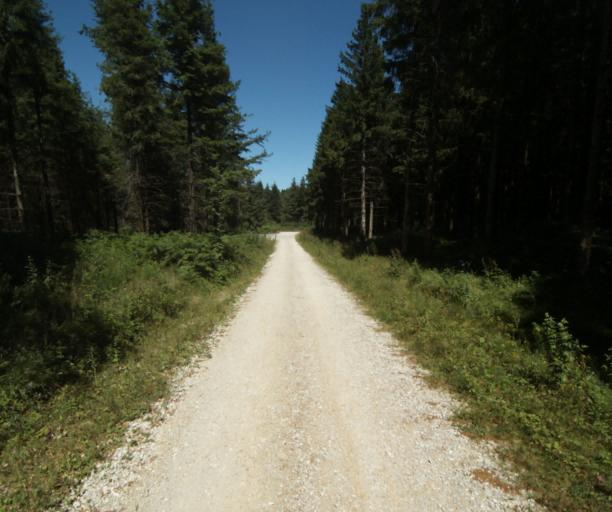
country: FR
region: Midi-Pyrenees
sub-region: Departement du Tarn
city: Dourgne
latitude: 43.4453
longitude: 2.1441
